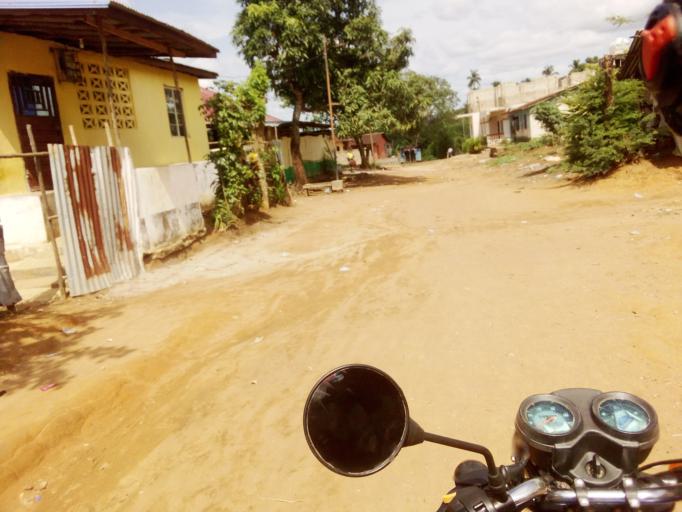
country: SL
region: Western Area
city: Waterloo
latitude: 8.3344
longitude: -13.0690
